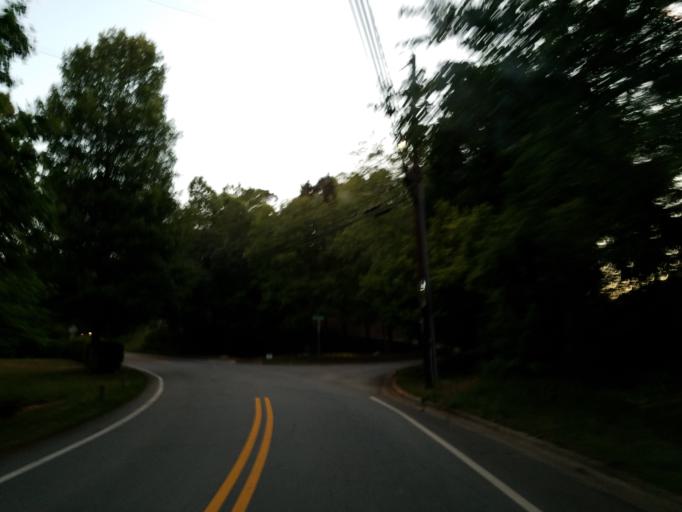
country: US
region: Georgia
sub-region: Fulton County
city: Sandy Springs
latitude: 33.8868
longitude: -84.4026
